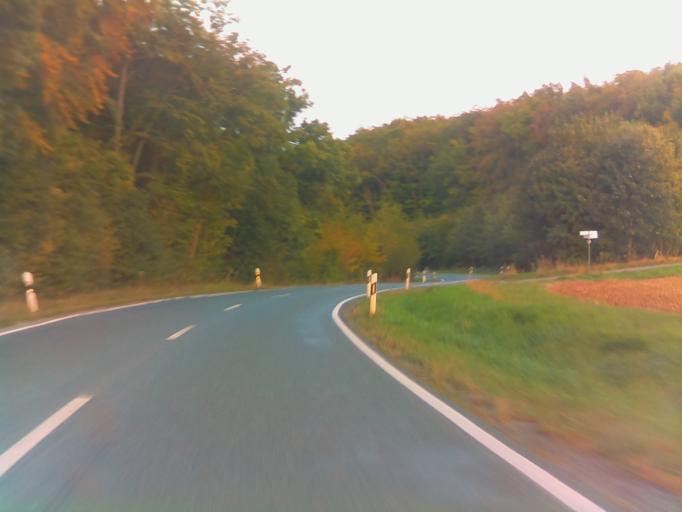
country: DE
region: Bavaria
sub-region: Regierungsbezirk Unterfranken
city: Ramsthal
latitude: 50.1483
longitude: 10.0957
